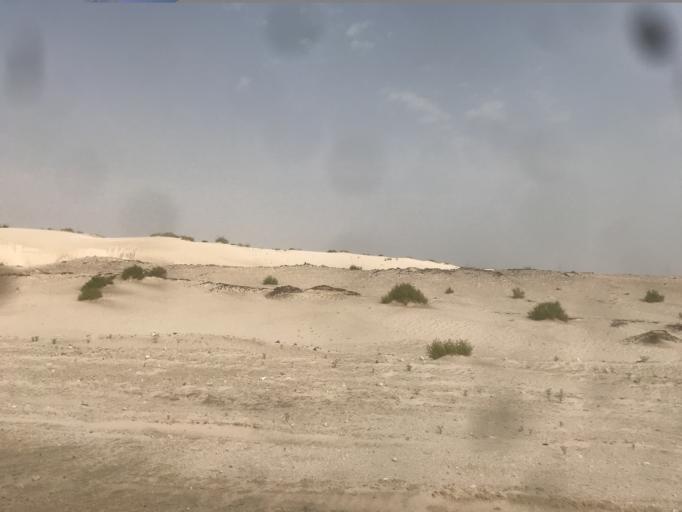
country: SA
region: Eastern Province
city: Abqaiq
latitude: 25.9068
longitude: 50.0006
